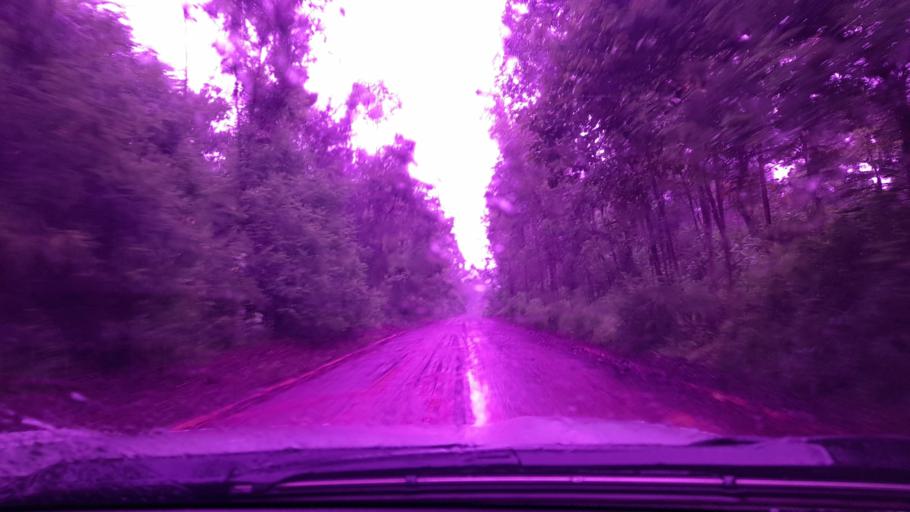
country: ET
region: Oromiya
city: Metu
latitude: 8.3283
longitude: 35.6032
